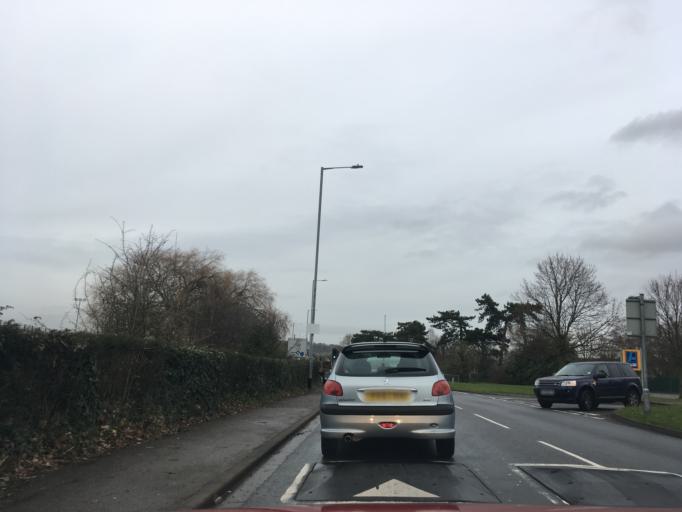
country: GB
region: Wales
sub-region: Newport
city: Nash
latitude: 51.5736
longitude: -2.9542
